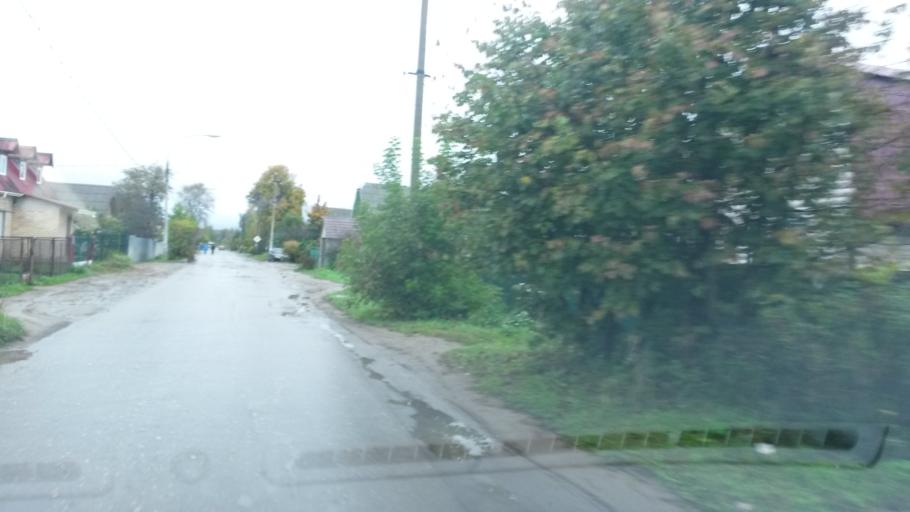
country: RU
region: Jaroslavl
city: Gavrilov-Yam
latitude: 57.3096
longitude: 39.8560
